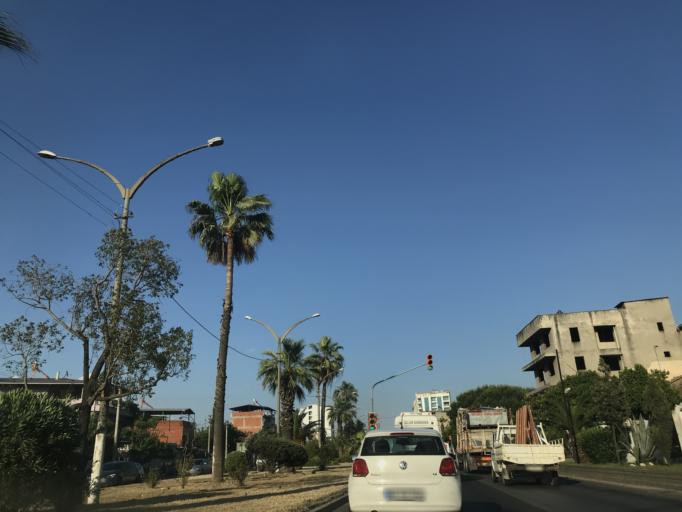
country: TR
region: Aydin
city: Umurlu
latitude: 37.8505
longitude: 27.9579
